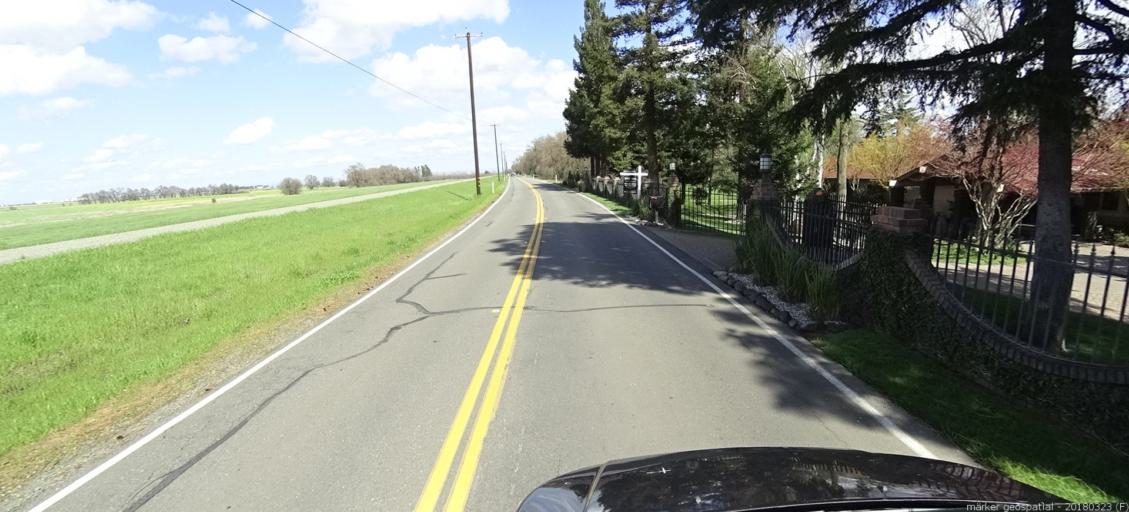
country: US
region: California
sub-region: Yolo County
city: West Sacramento
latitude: 38.6447
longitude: -121.5867
